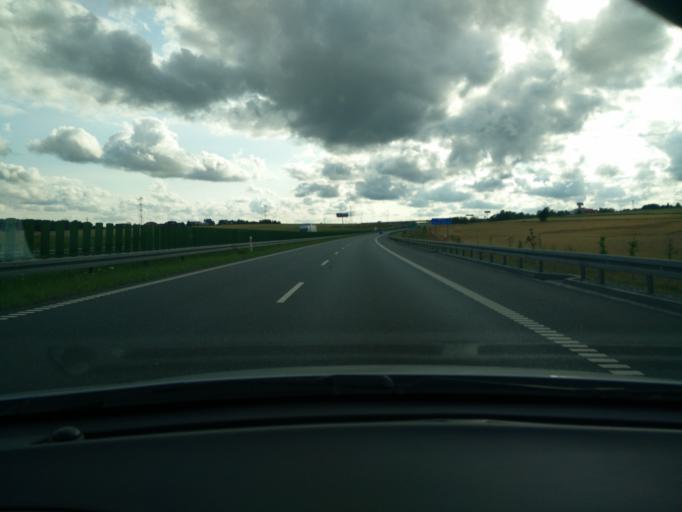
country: PL
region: Pomeranian Voivodeship
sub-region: Powiat gdanski
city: Rotmanka
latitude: 54.2908
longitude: 18.6101
